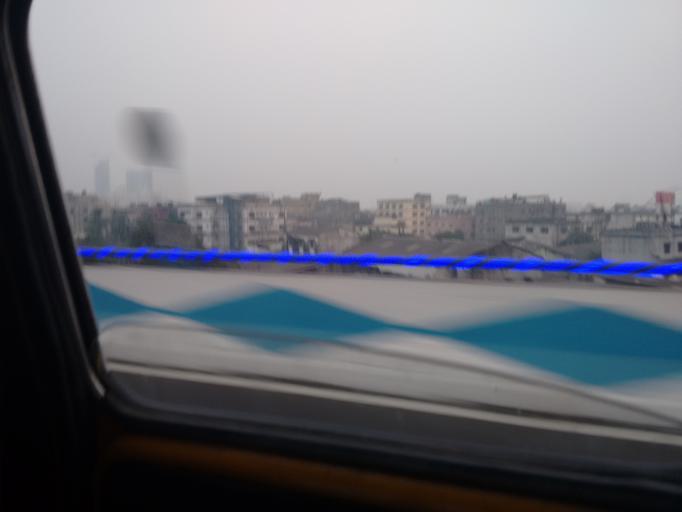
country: IN
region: West Bengal
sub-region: Kolkata
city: Kolkata
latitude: 22.5410
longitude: 88.3831
